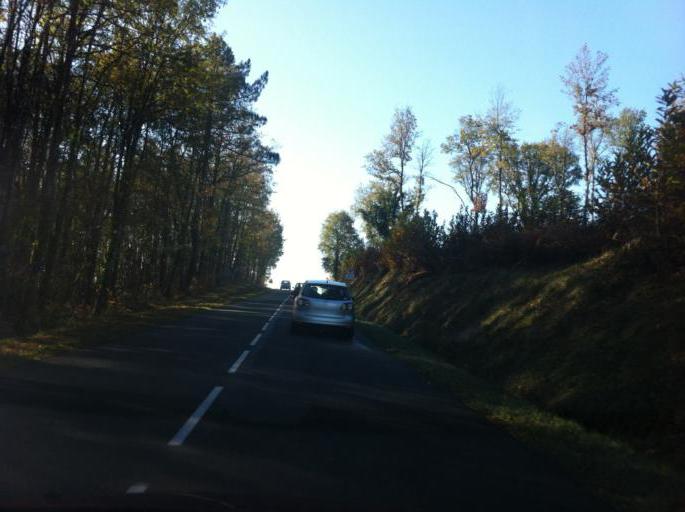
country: FR
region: Aquitaine
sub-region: Departement de la Dordogne
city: Saint-Aulaye
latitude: 45.2668
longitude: 0.1831
